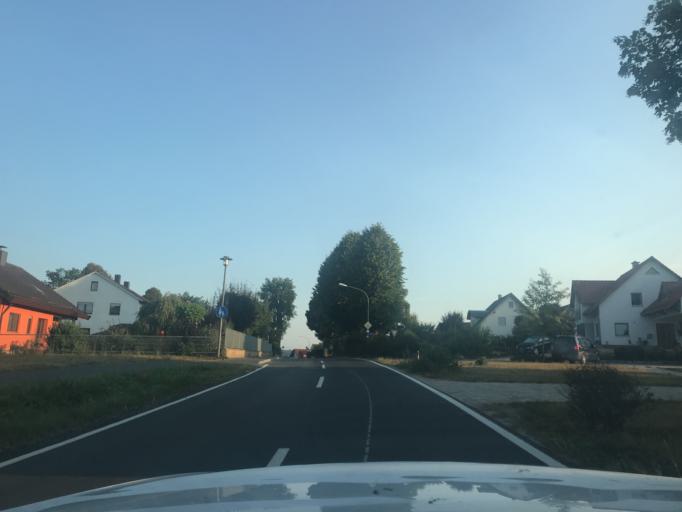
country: DE
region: Bavaria
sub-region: Upper Franconia
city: Pegnitz
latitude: 49.7135
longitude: 11.5753
